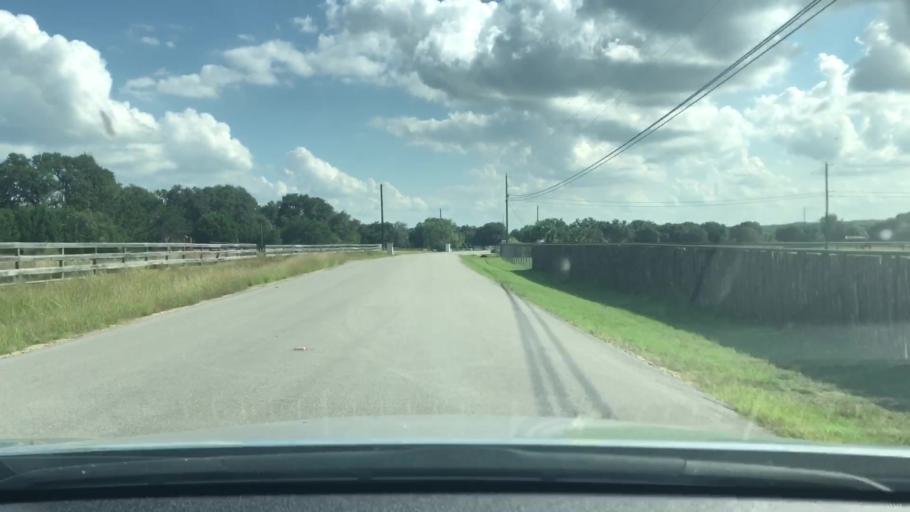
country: US
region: Texas
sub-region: Bexar County
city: Fair Oaks Ranch
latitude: 29.7666
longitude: -98.6311
